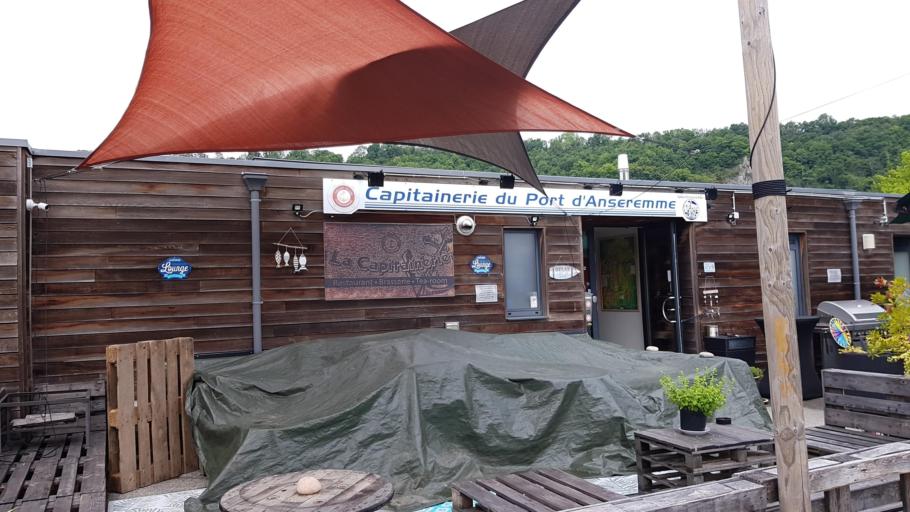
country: BE
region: Wallonia
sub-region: Province de Namur
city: Dinant
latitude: 50.2393
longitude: 4.8951
